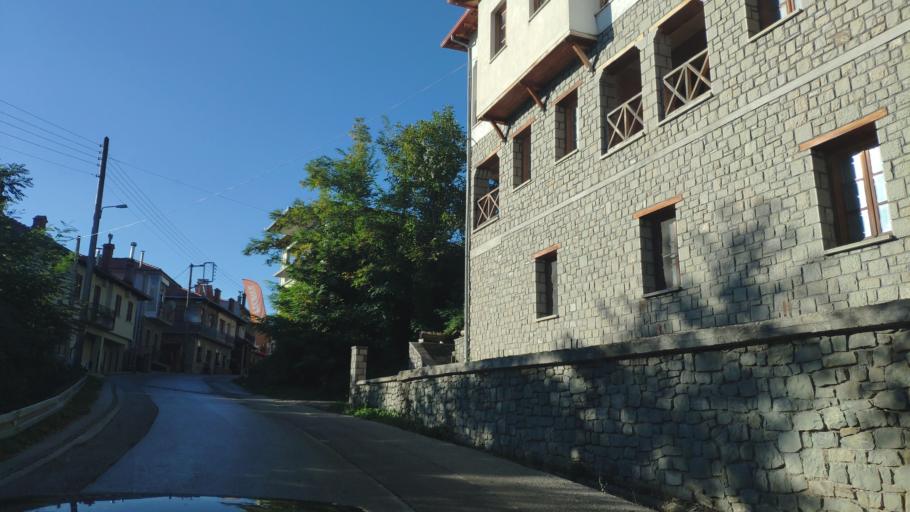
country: GR
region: Epirus
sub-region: Nomos Ioanninon
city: Metsovo
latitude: 39.7738
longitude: 21.1787
